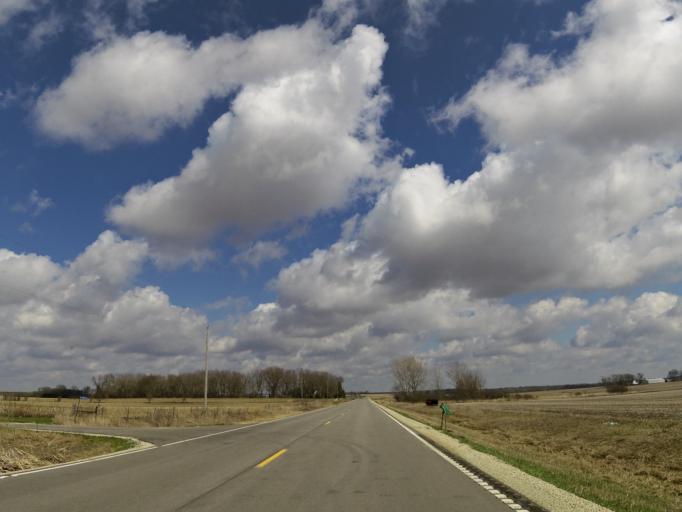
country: US
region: Minnesota
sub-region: Dodge County
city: Dodge Center
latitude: 44.0880
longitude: -92.8627
